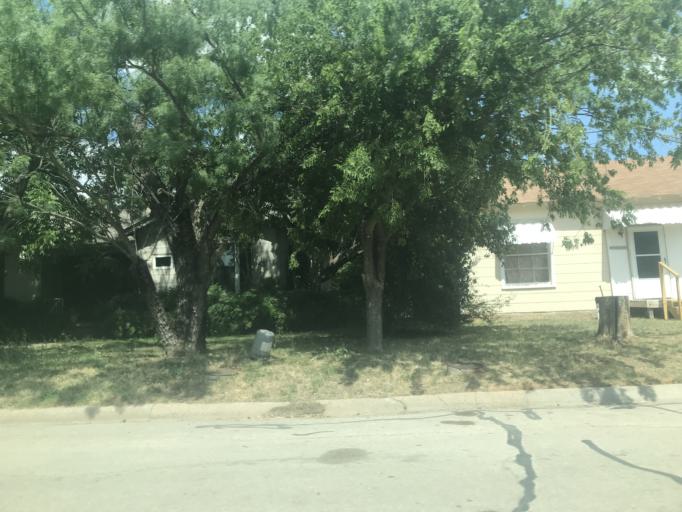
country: US
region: Texas
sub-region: Taylor County
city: Abilene
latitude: 32.4265
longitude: -99.7526
